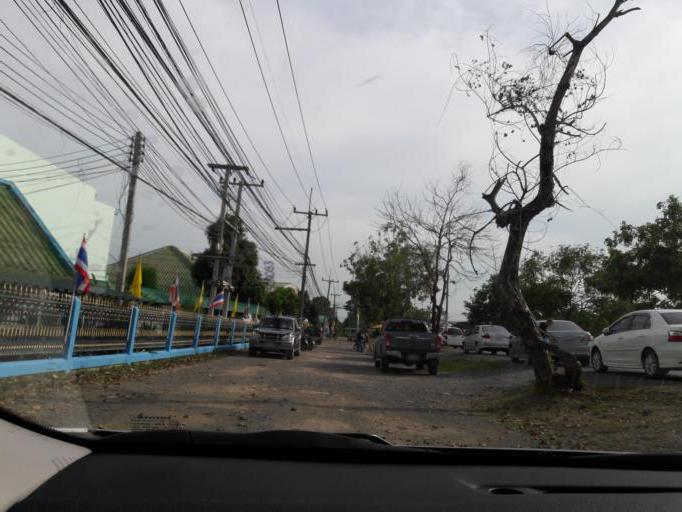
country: TH
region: Ang Thong
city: Ang Thong
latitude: 14.5847
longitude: 100.4442
